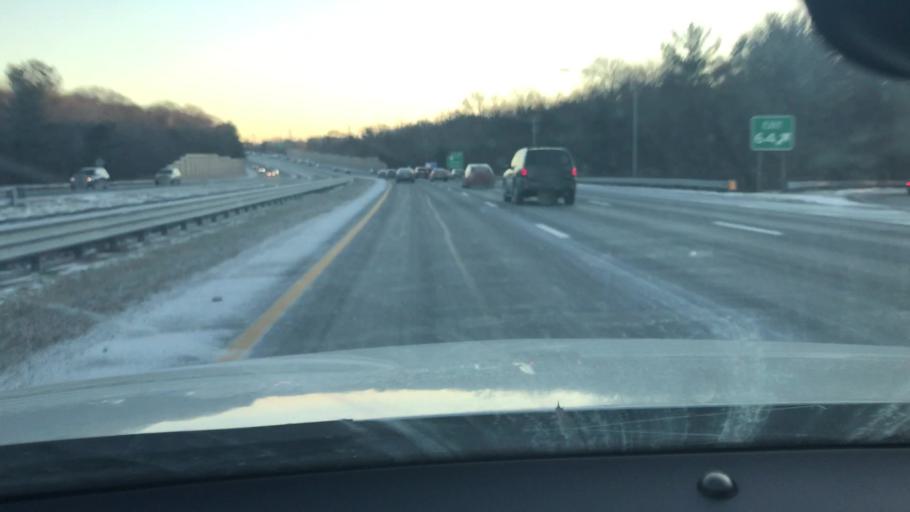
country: US
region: New Jersey
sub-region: Mercer County
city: Mercerville
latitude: 40.2416
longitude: -74.7016
